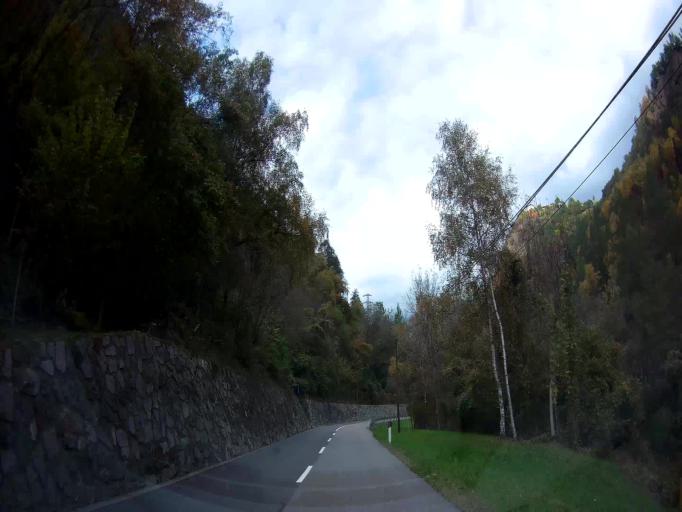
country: IT
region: Trentino-Alto Adige
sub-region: Bolzano
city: Certosa
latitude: 46.6819
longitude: 10.9351
